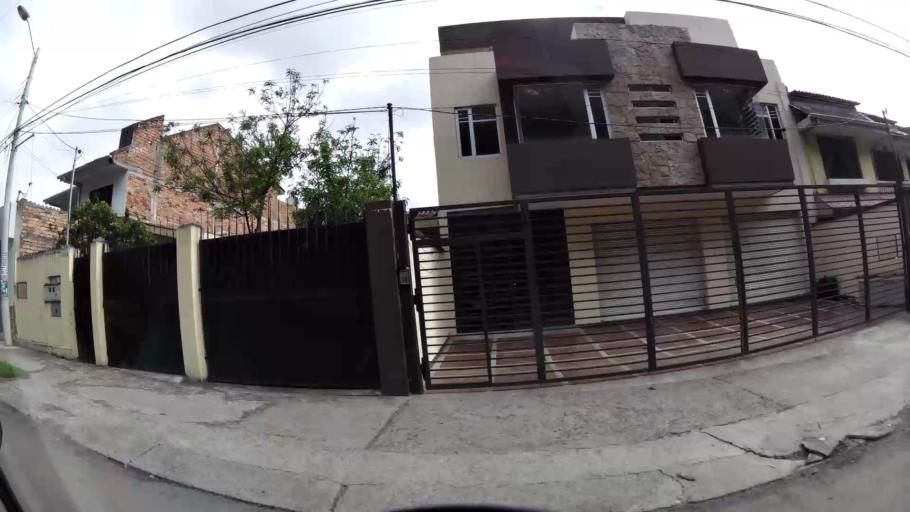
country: EC
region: Azuay
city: Cuenca
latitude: -2.9079
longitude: -78.9858
